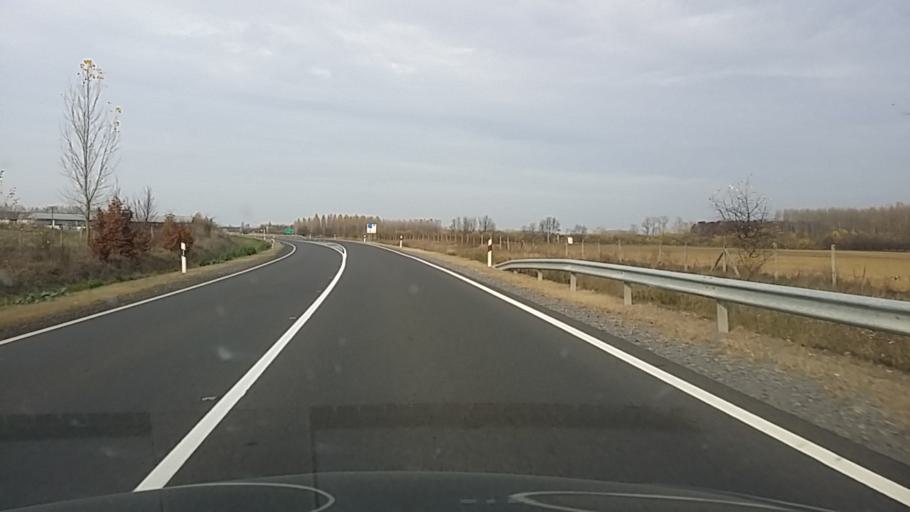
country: HU
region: Szabolcs-Szatmar-Bereg
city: Nyirpazony
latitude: 48.0089
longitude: 21.8444
